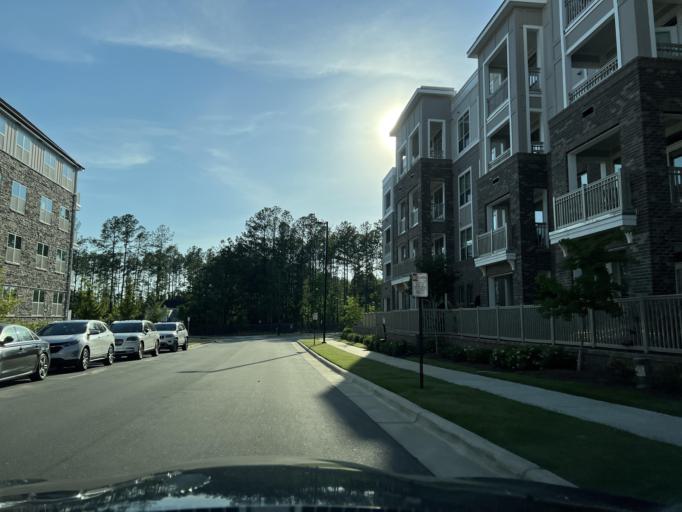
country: US
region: North Carolina
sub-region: Wake County
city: Green Level
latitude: 35.8307
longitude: -78.8826
